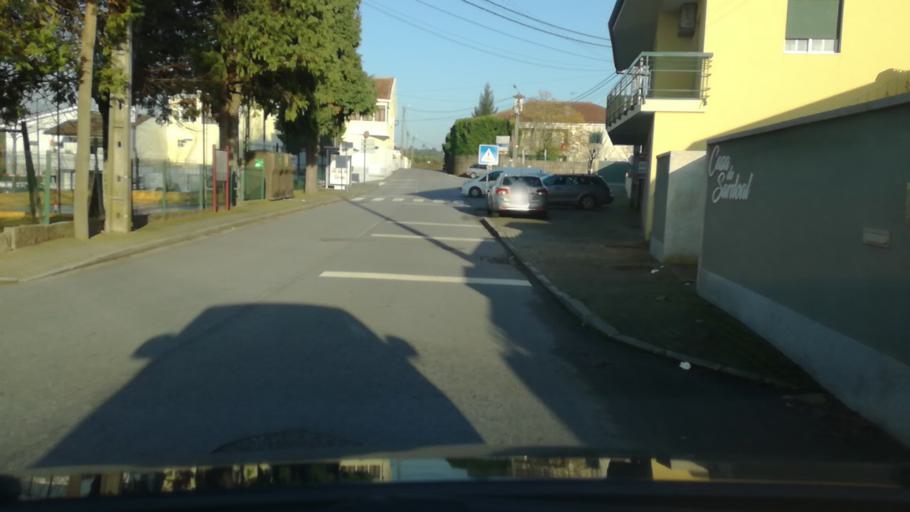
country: PT
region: Braga
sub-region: Vila Nova de Famalicao
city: Ferreiros
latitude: 41.3513
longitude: -8.5228
